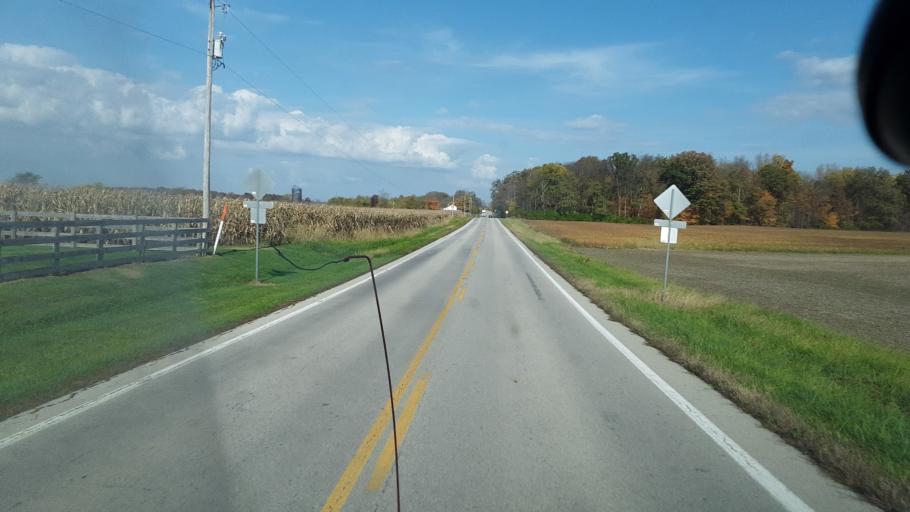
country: US
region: Ohio
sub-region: Clinton County
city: Sabina
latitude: 39.5314
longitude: -83.7023
